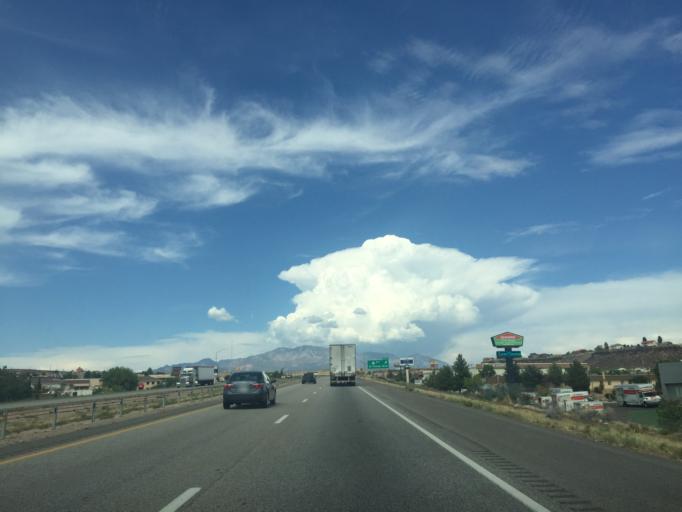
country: US
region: Utah
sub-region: Washington County
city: Saint George
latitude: 37.1035
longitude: -113.5603
